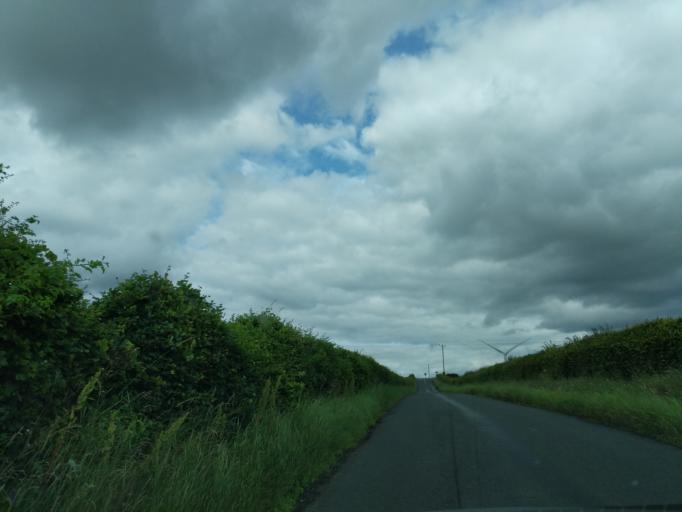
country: GB
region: Scotland
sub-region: South Lanarkshire
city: Larkhall
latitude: 55.7027
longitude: -3.9575
